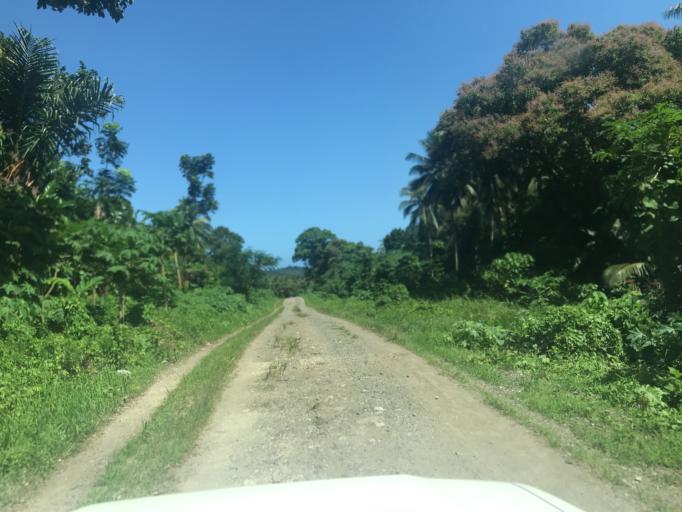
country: VU
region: Sanma
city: Luganville
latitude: -15.6023
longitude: 166.7828
